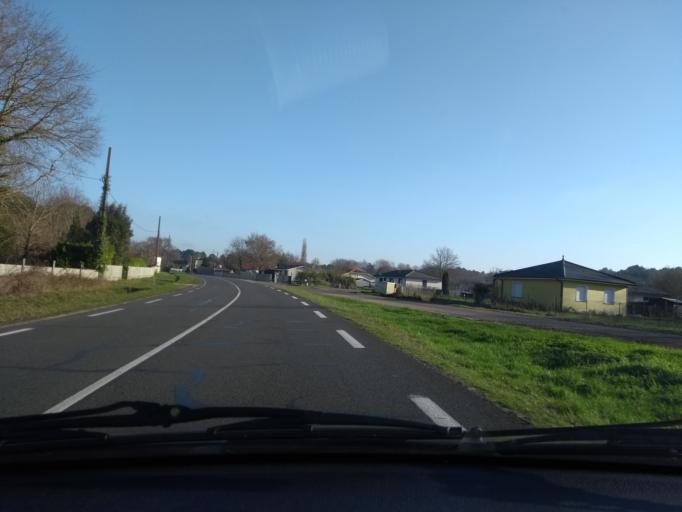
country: FR
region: Aquitaine
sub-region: Departement de la Gironde
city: Mios
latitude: 44.5969
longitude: -0.9111
